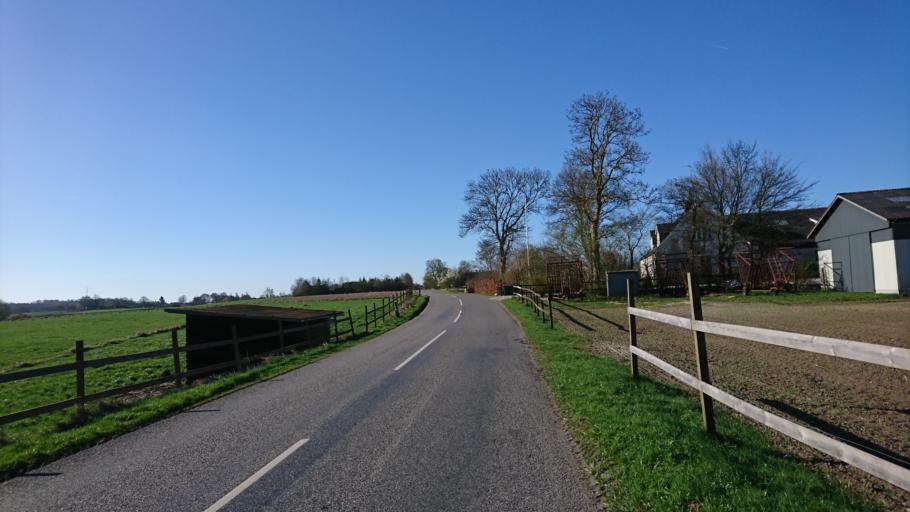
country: DK
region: Capital Region
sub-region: Frederikssund Kommune
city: Skibby
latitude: 55.7309
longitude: 11.9285
